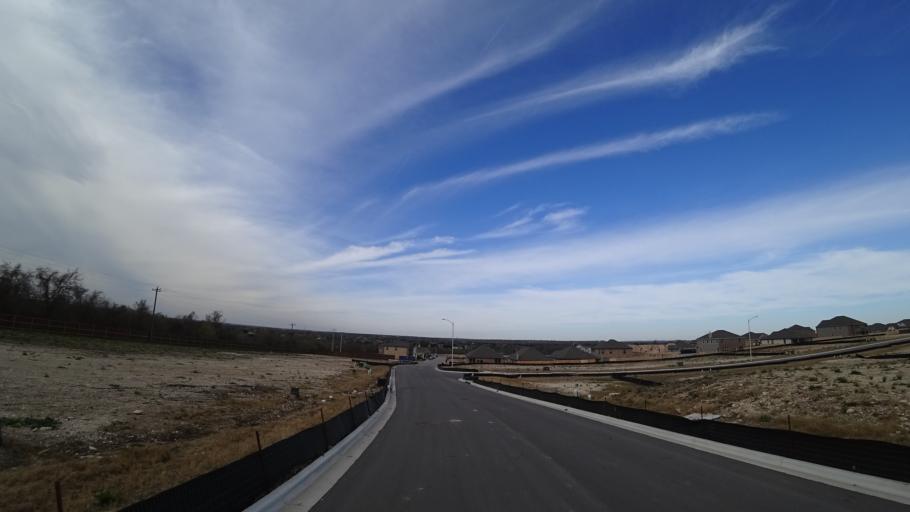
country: US
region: Texas
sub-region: Travis County
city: Onion Creek
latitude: 30.1582
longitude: -97.7312
